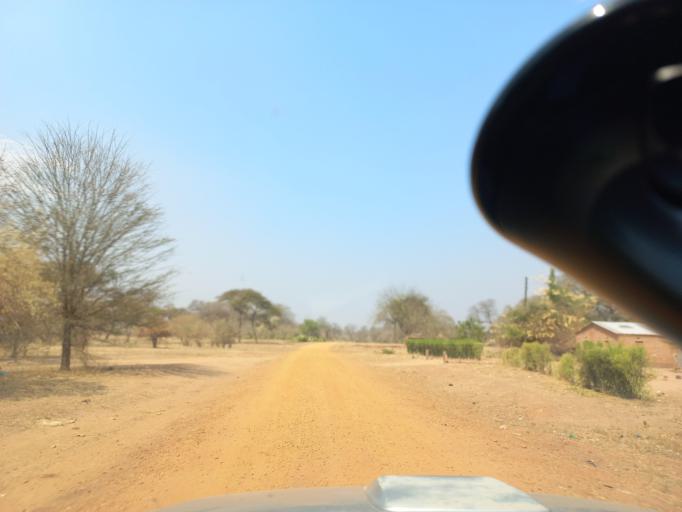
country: ZW
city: Chirundu
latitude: -15.9472
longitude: 28.8109
